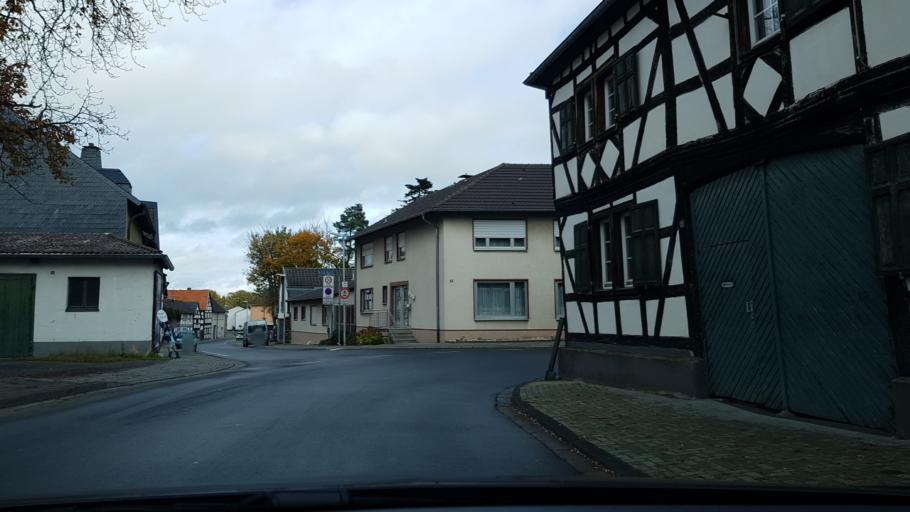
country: DE
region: North Rhine-Westphalia
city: Meckenheim
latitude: 50.5945
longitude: 7.0068
